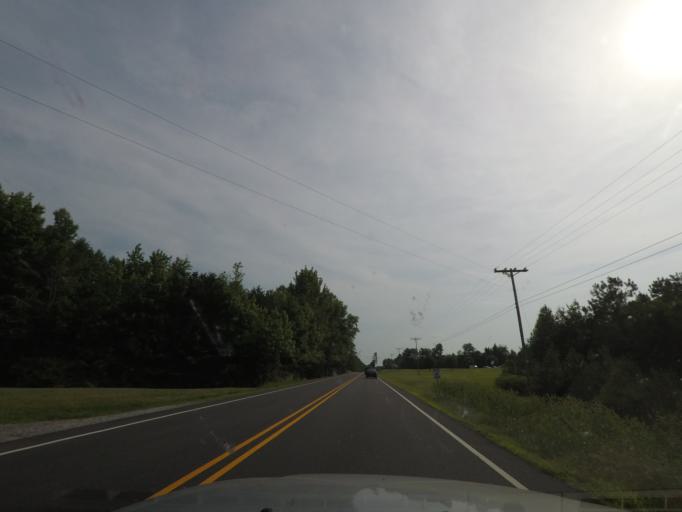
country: US
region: Virginia
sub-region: Prince Edward County
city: Hampden Sydney
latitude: 37.1205
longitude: -78.4563
